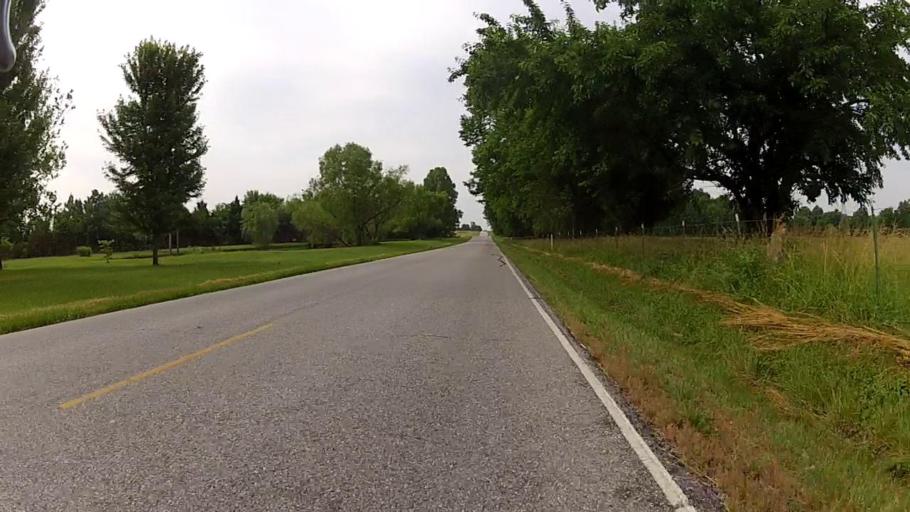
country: US
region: Kansas
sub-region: Cherokee County
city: Baxter Springs
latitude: 37.0845
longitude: -94.7224
